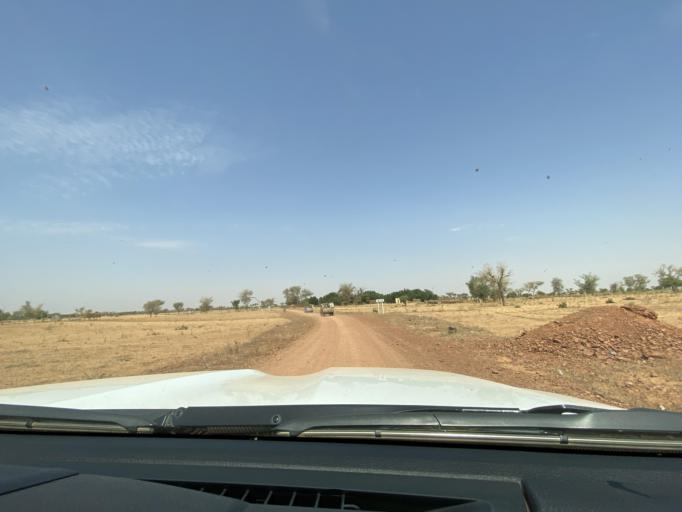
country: NE
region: Dosso
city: Birnin Gaoure
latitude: 13.2406
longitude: 2.8668
